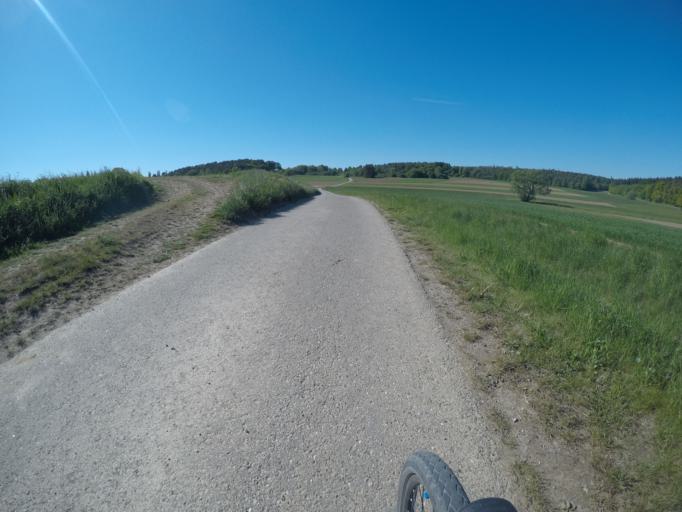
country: DE
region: Baden-Wuerttemberg
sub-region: Karlsruhe Region
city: Heimsheim
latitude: 48.8200
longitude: 8.8545
